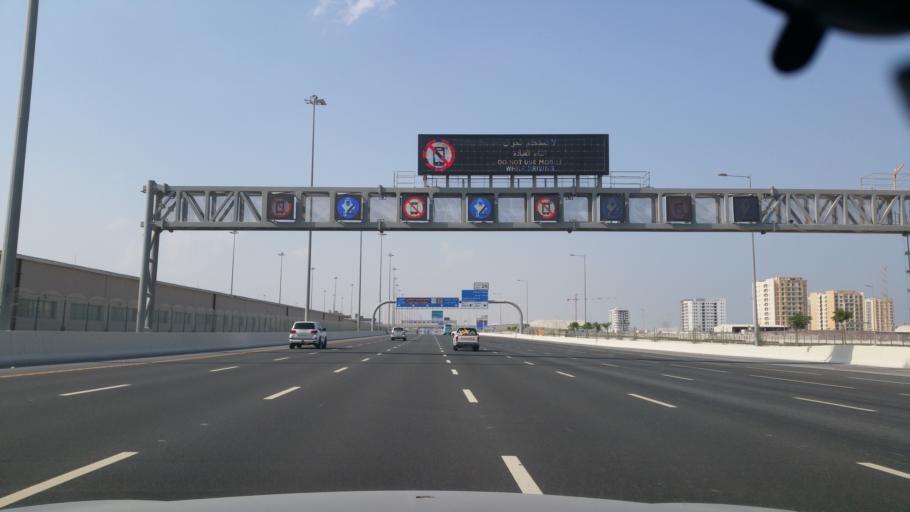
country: QA
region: Baladiyat Umm Salal
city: Umm Salal Muhammad
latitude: 25.4197
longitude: 51.4871
